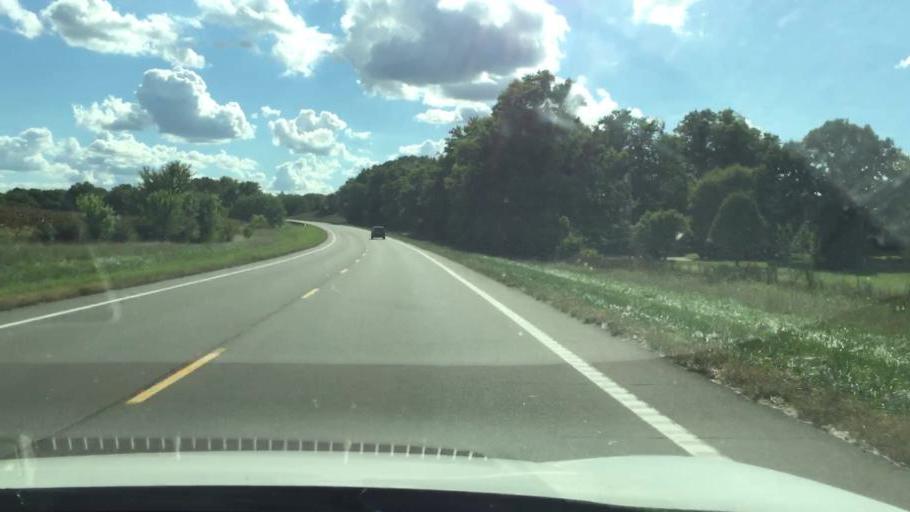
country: US
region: Ohio
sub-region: Clark County
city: Northridge
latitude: 40.0002
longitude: -83.7252
